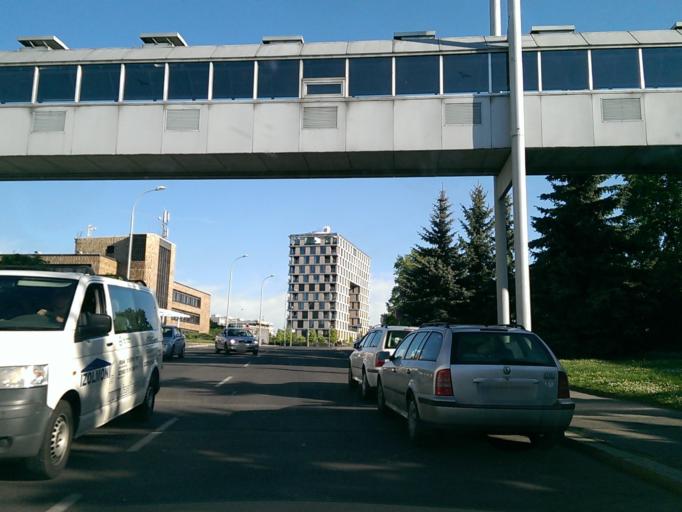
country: CZ
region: Praha
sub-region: Praha 2
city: Vysehrad
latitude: 50.0509
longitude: 14.4277
